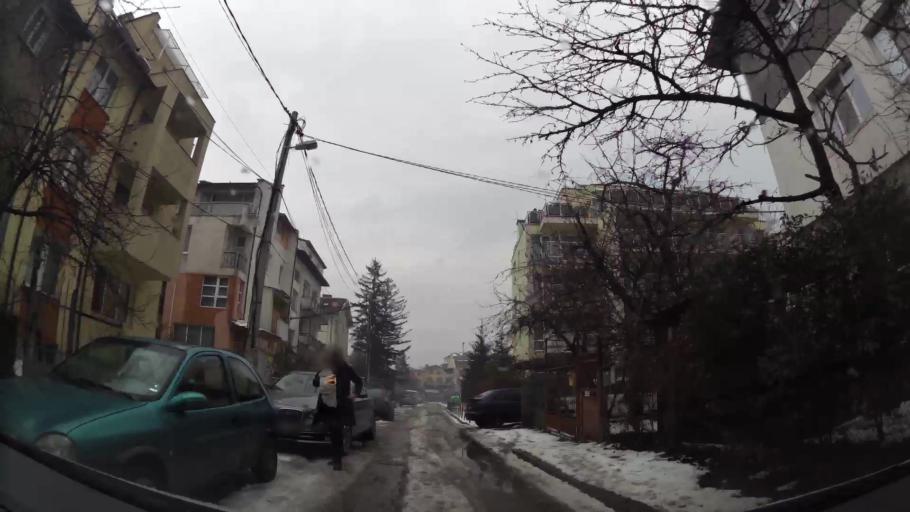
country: BG
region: Sofia-Capital
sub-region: Stolichna Obshtina
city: Sofia
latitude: 42.6810
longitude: 23.2643
